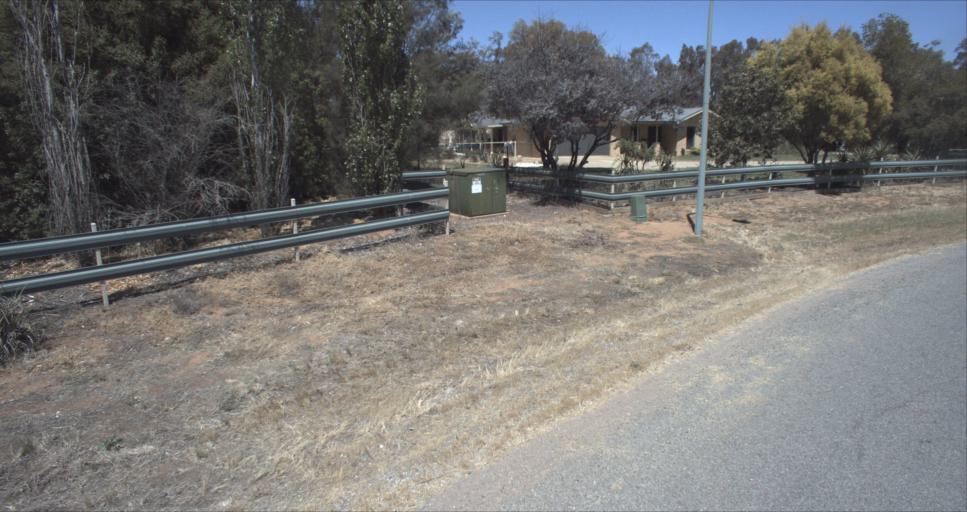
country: AU
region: New South Wales
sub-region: Leeton
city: Leeton
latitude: -34.5296
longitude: 146.3985
